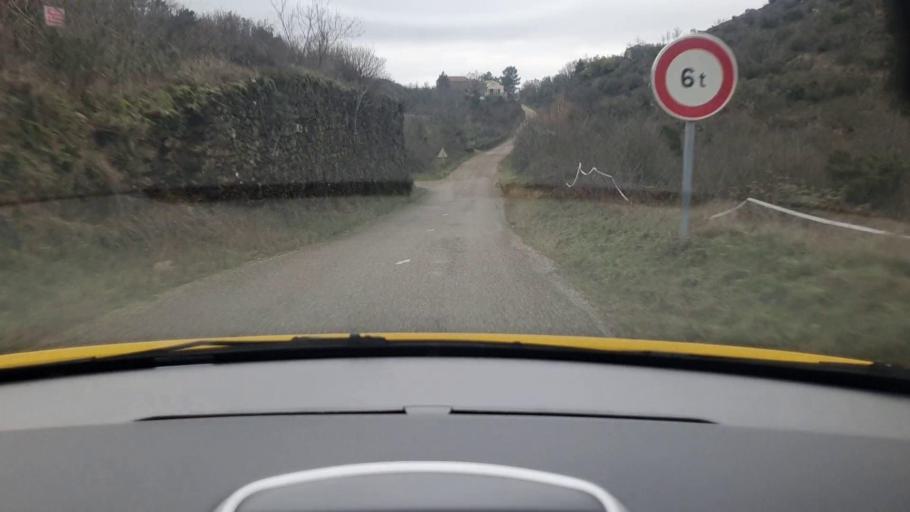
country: FR
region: Languedoc-Roussillon
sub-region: Departement du Gard
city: Besseges
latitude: 44.3092
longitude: 4.1440
